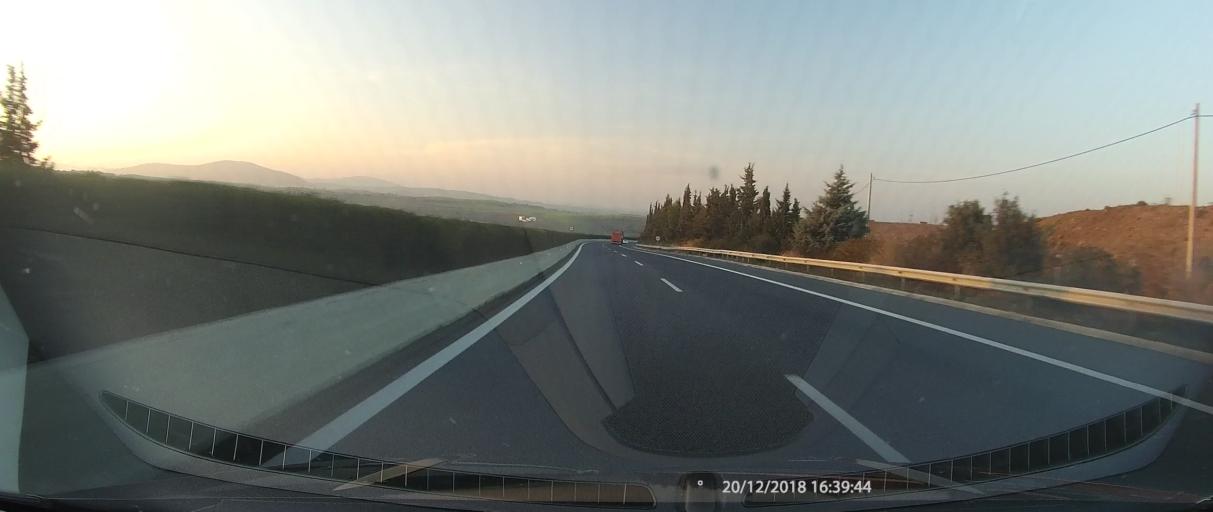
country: GR
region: Thessaly
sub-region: Nomos Magnisias
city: Velestino
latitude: 39.3635
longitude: 22.7727
